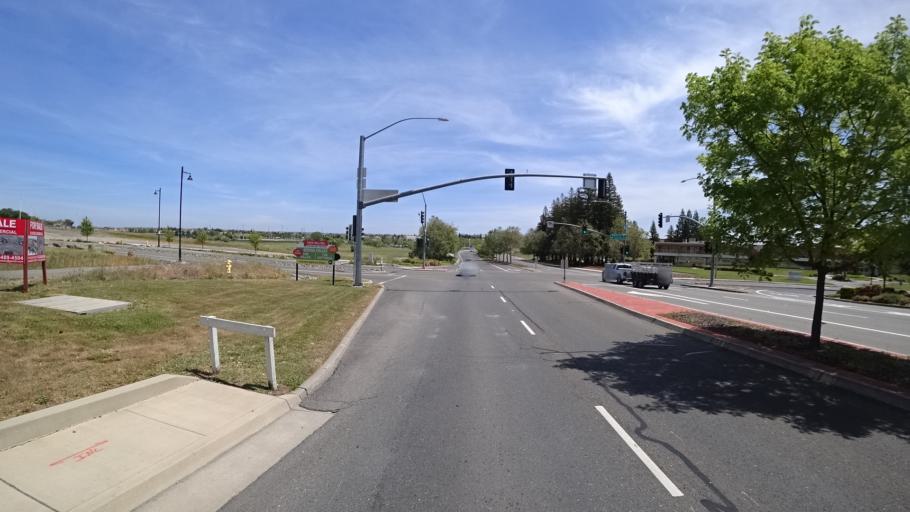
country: US
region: California
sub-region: Placer County
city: Rocklin
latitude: 38.8173
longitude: -121.2928
